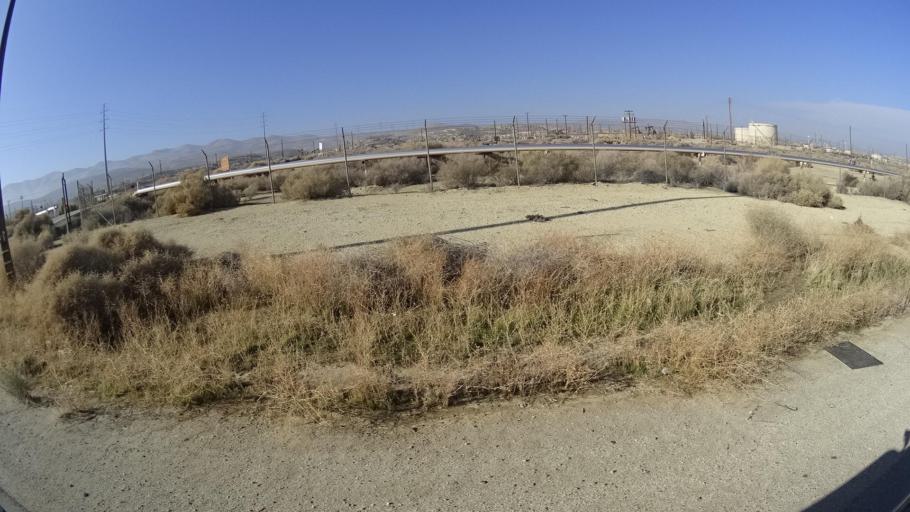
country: US
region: California
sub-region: Kern County
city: Taft Heights
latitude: 35.2106
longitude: -119.5982
